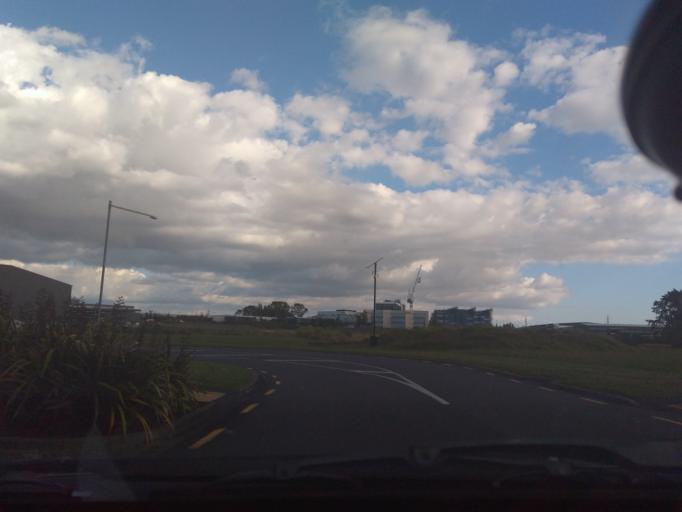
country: NZ
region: Auckland
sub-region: Auckland
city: Tamaki
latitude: -36.9331
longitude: 174.8724
